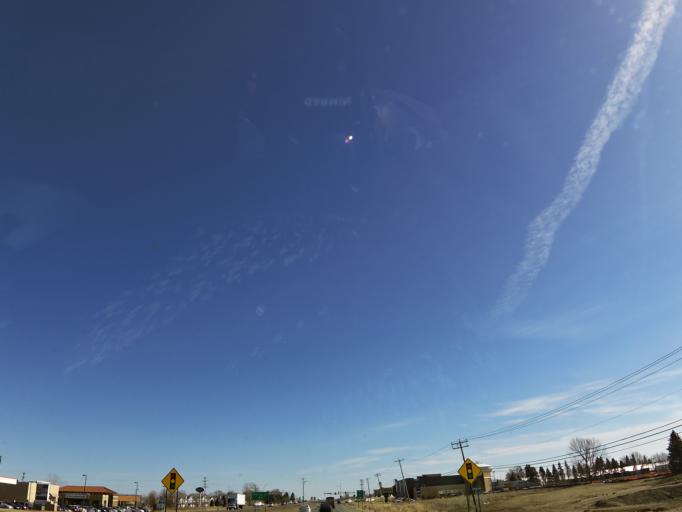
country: US
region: Minnesota
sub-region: Hennepin County
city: Plymouth
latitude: 45.0340
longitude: -93.5106
